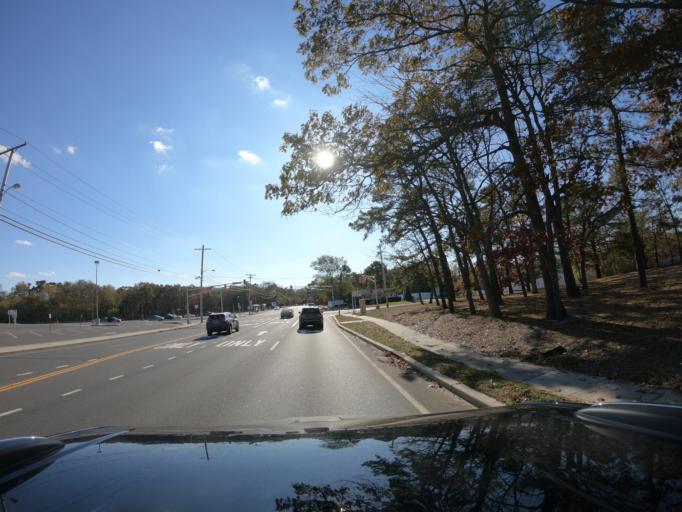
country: US
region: New Jersey
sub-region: Monmouth County
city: Ramtown
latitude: 40.0955
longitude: -74.1457
